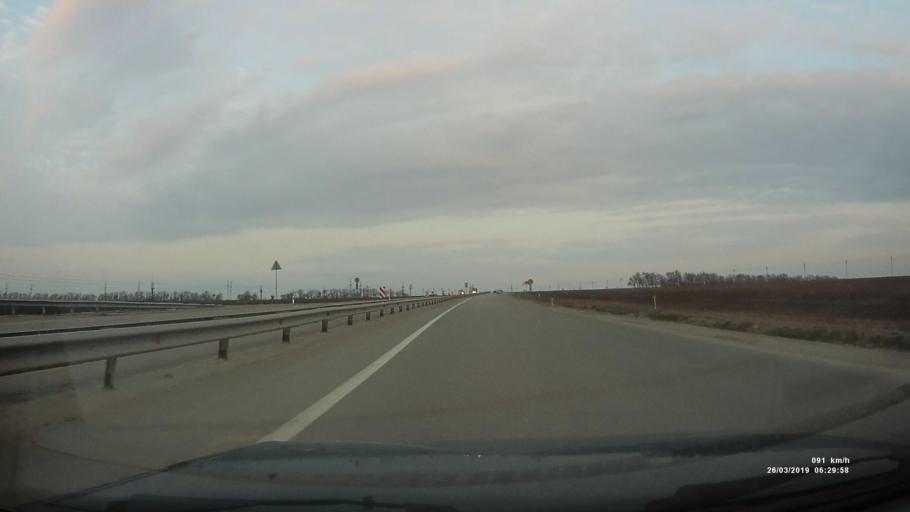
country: RU
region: Rostov
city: Kalinin
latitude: 47.2679
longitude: 39.5623
